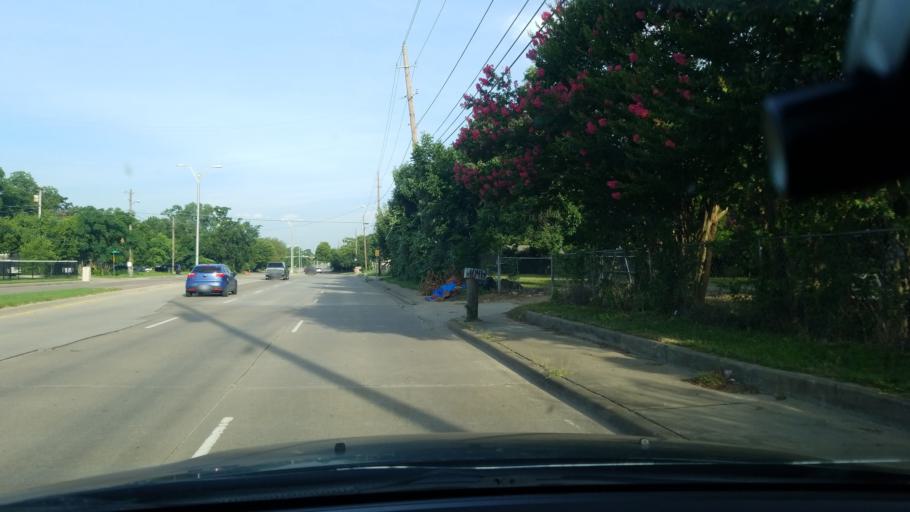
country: US
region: Texas
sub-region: Dallas County
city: Balch Springs
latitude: 32.7196
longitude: -96.6446
